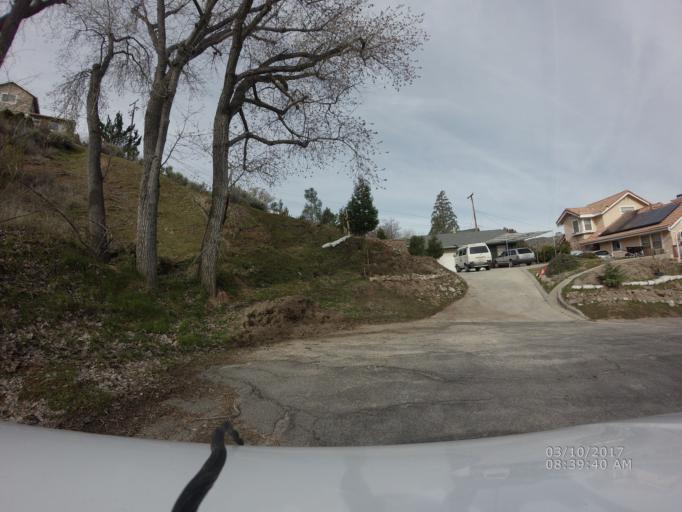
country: US
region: California
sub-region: Los Angeles County
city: Green Valley
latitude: 34.6614
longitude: -118.3948
